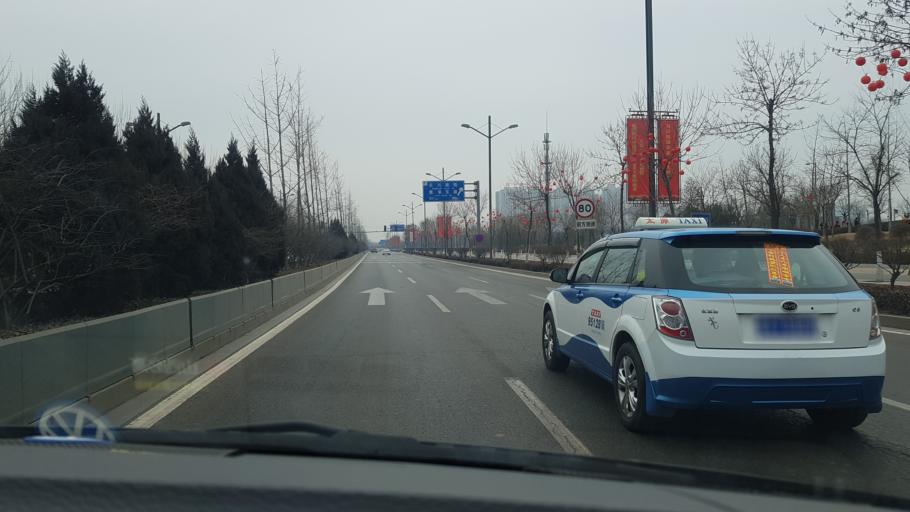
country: CN
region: Shanxi Sheng
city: Qianfeng
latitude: 37.8033
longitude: 112.5306
